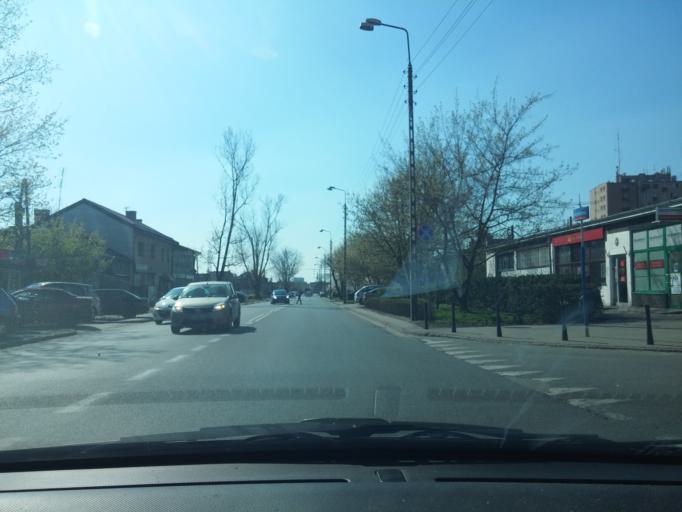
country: PL
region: Masovian Voivodeship
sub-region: Warszawa
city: Rembertow
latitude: 52.2383
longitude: 21.1478
